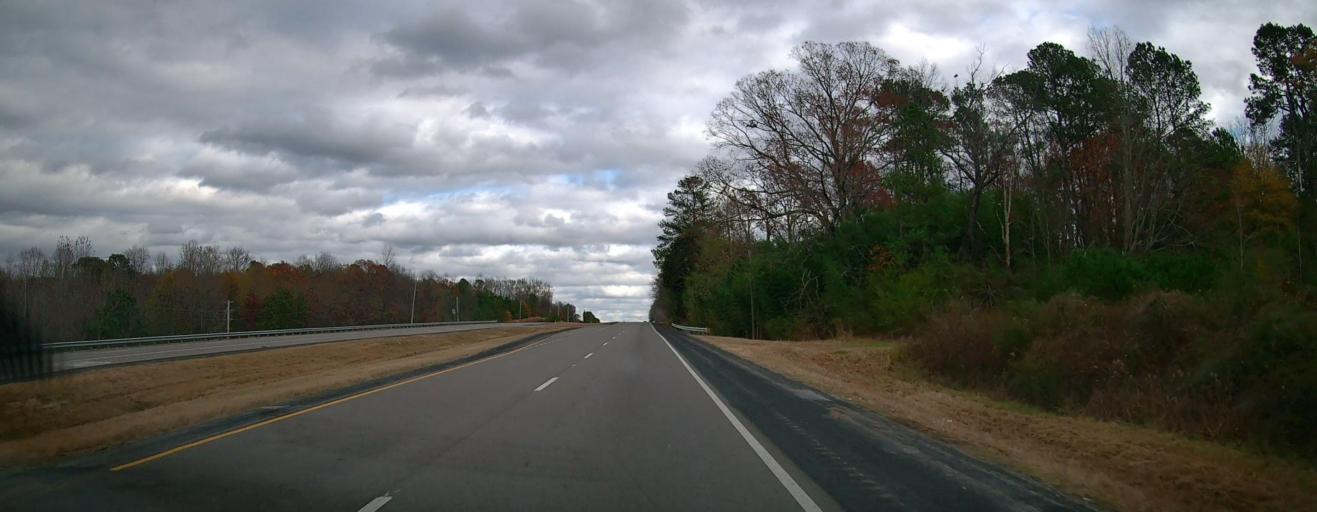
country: US
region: Alabama
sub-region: Cullman County
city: Cullman
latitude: 34.2390
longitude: -86.9466
